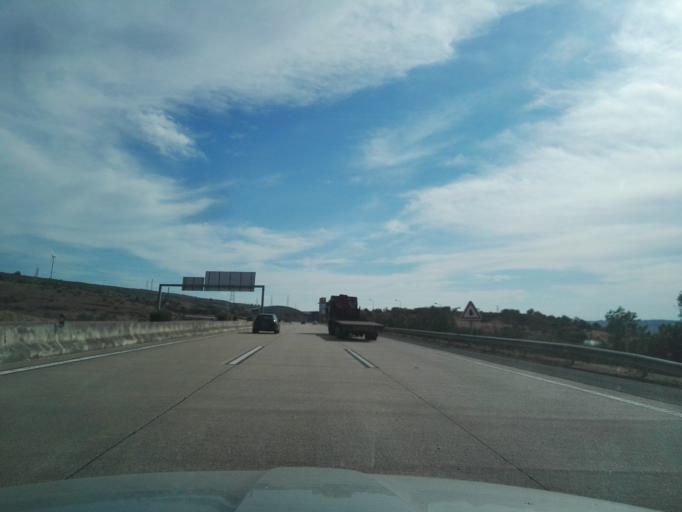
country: PT
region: Lisbon
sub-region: Loures
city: Santo Antao do Tojal
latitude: 38.8677
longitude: -9.1419
